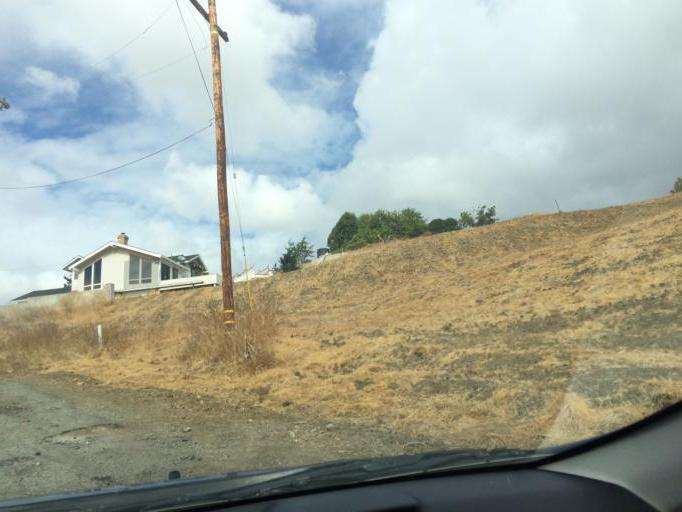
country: US
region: California
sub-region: Santa Clara County
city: East Foothills
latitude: 37.3374
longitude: -121.7661
